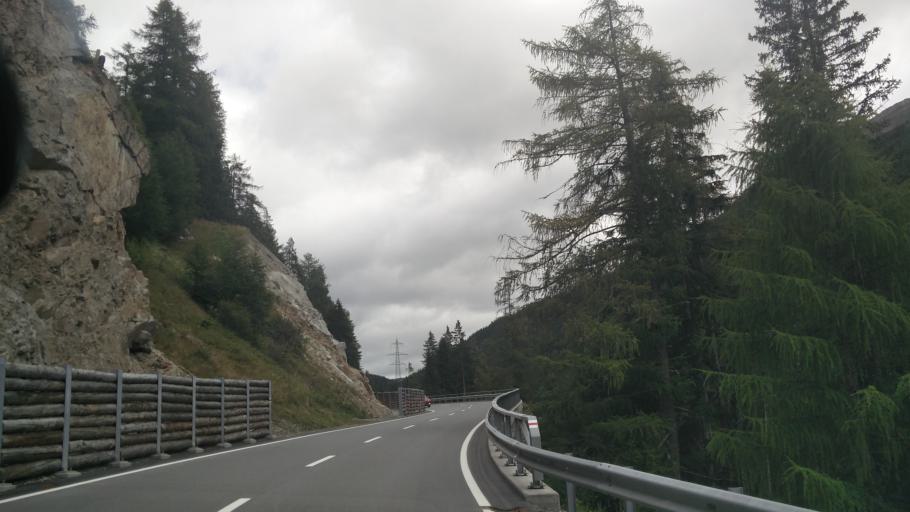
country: CH
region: Grisons
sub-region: Inn District
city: Zernez
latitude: 46.6962
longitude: 10.1169
